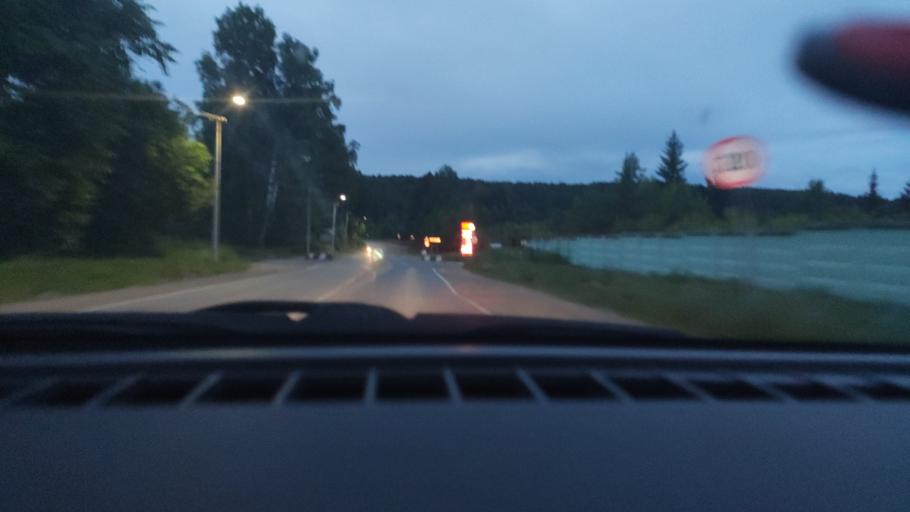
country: RU
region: Perm
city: Zvezdnyy
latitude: 57.7345
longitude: 56.3250
